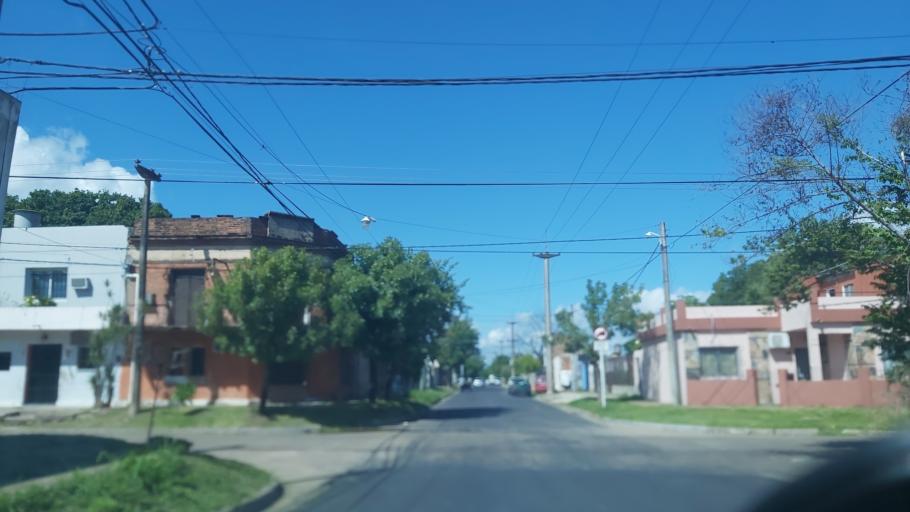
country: AR
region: Corrientes
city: Corrientes
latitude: -27.4791
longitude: -58.8475
